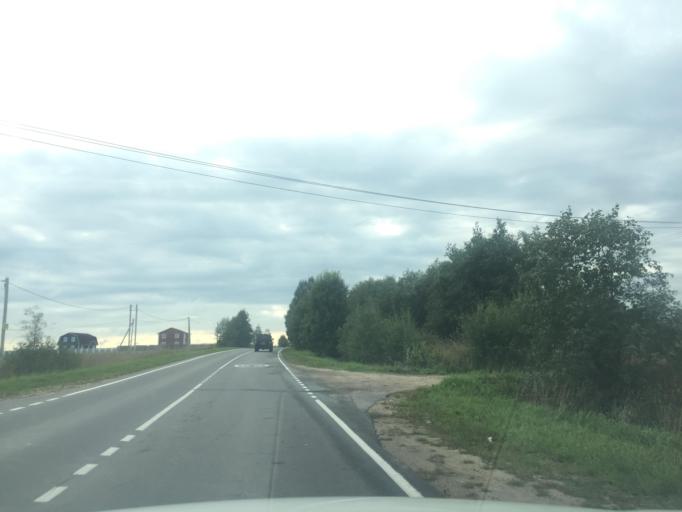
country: RU
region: Leningrad
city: Siverskiy
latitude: 59.3388
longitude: 30.0258
